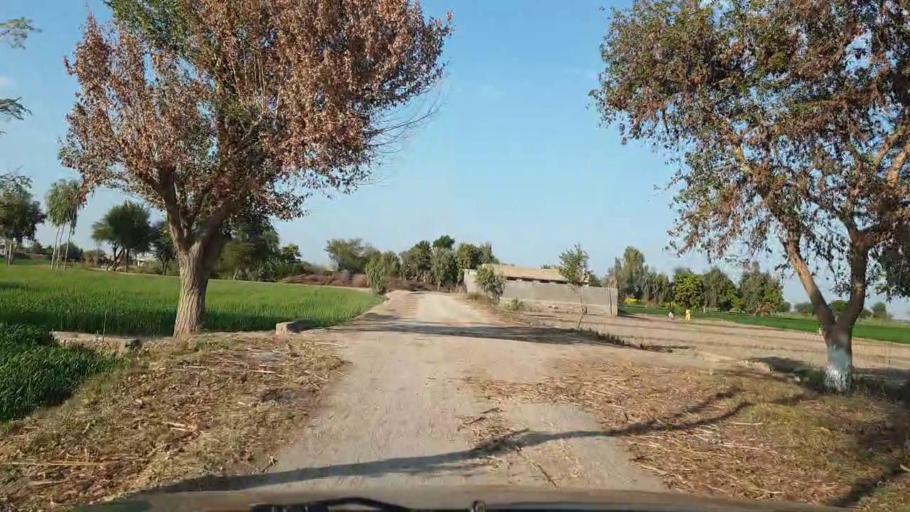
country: PK
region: Sindh
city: Sinjhoro
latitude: 25.9975
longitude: 68.7398
